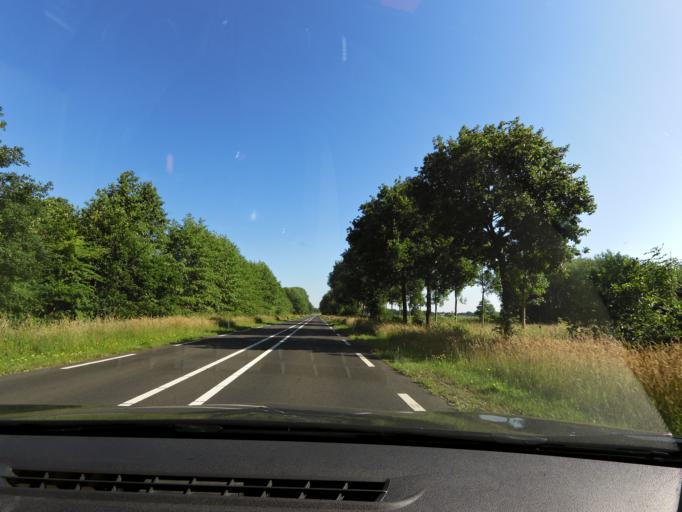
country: NL
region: Overijssel
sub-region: Gemeente Twenterand
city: Den Ham
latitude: 52.4482
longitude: 6.4230
